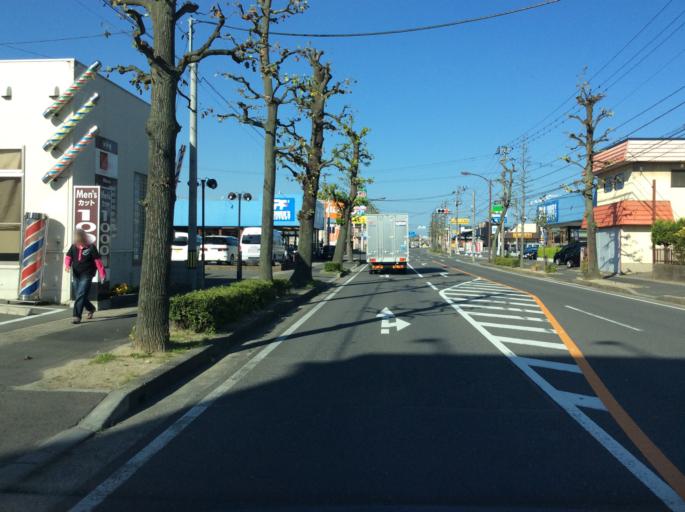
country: JP
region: Fukushima
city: Koriyama
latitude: 37.3754
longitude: 140.3839
